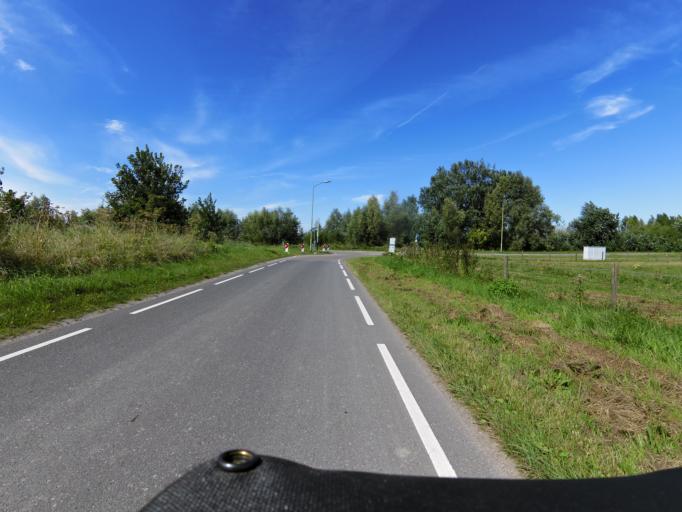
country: NL
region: South Holland
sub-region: Gemeente Sliedrecht
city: Sliedrecht
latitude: 51.7785
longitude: 4.7667
